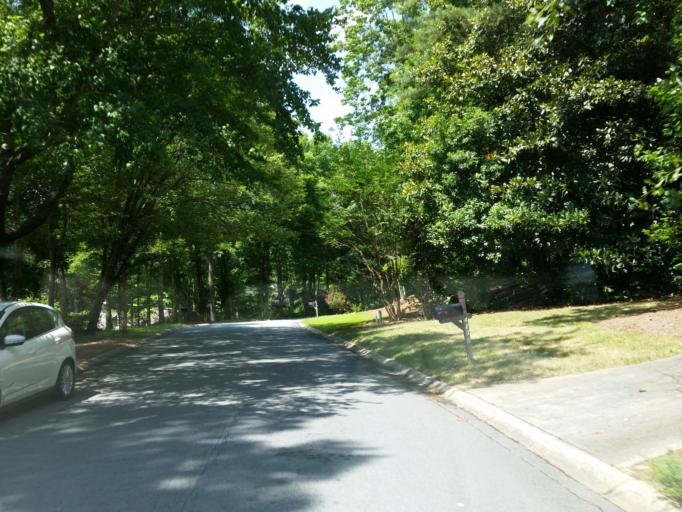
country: US
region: Georgia
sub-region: Fulton County
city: Roswell
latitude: 34.0479
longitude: -84.4297
